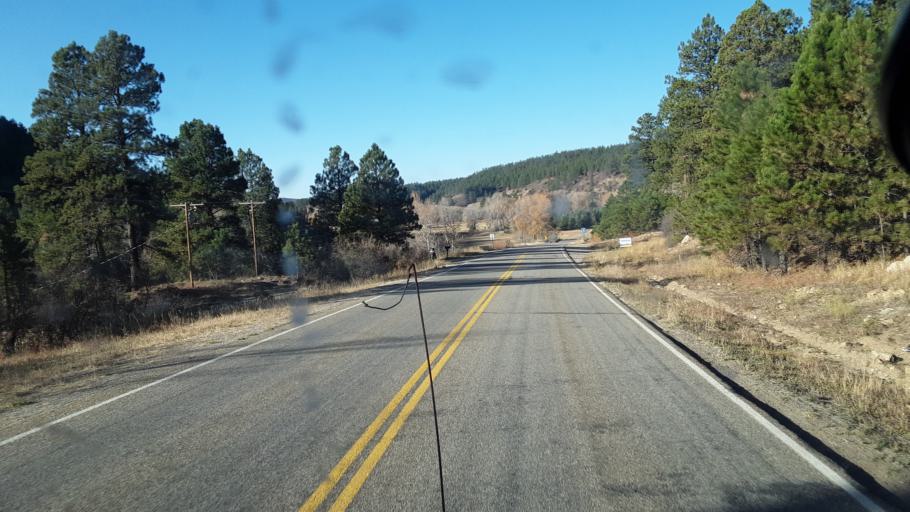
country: US
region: Colorado
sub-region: La Plata County
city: Durango
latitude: 37.3261
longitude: -107.7524
